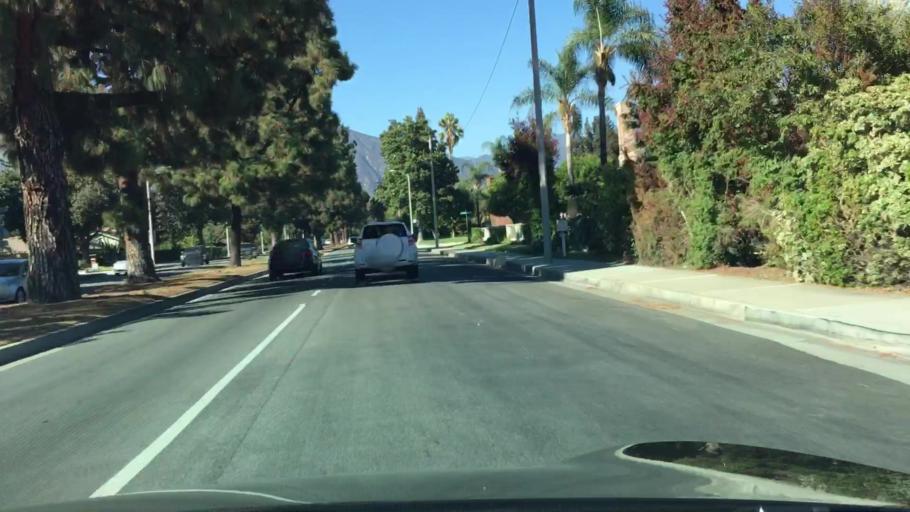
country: US
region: California
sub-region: Los Angeles County
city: Arcadia
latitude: 34.1254
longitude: -118.0311
